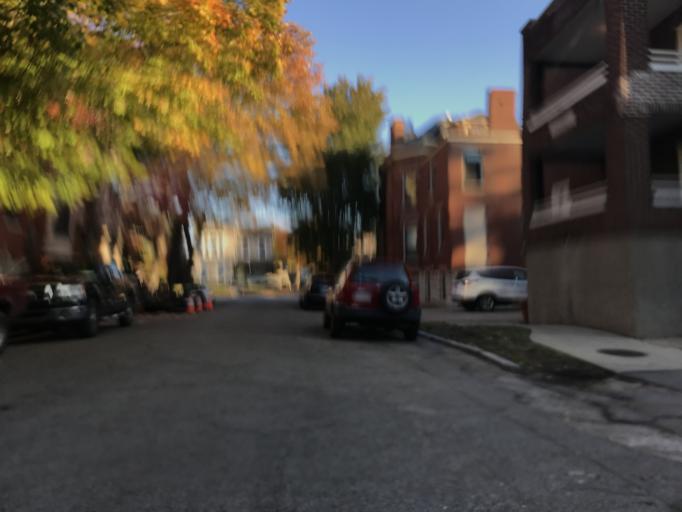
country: US
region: Kentucky
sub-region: Jefferson County
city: Louisville
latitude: 38.2435
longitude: -85.7299
